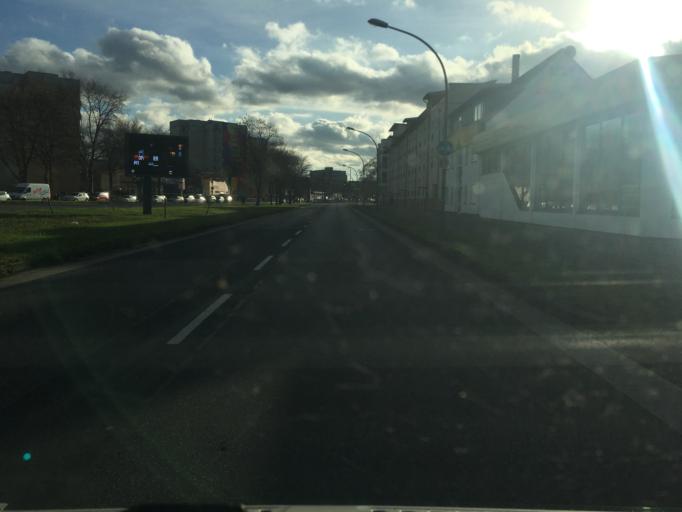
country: DE
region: North Rhine-Westphalia
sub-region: Regierungsbezirk Koln
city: Muelheim
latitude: 50.9750
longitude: 7.0051
